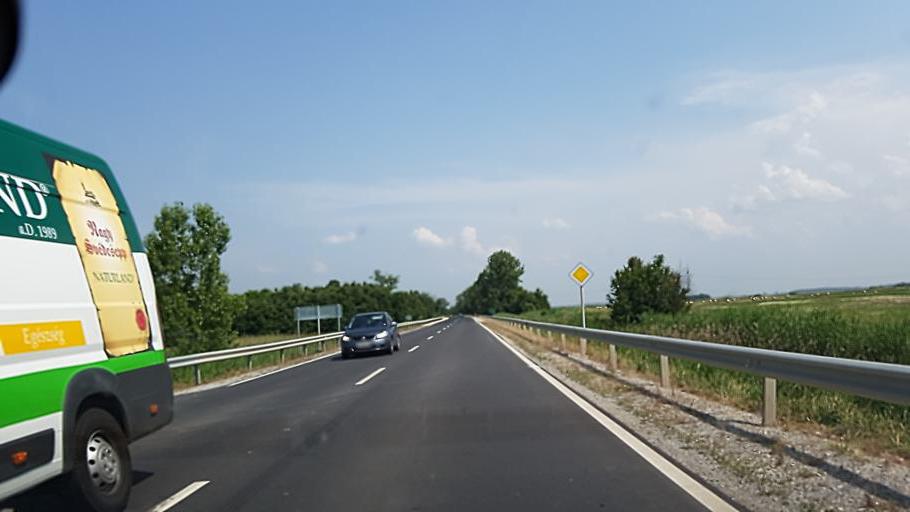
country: HU
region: Heves
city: Poroszlo
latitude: 47.6677
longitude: 20.5641
